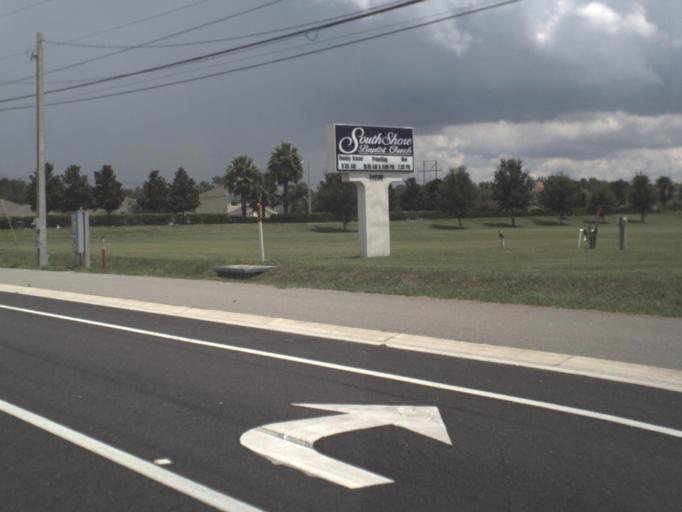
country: US
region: Florida
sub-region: Hillsborough County
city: Sun City Center
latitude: 27.7755
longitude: -82.3348
